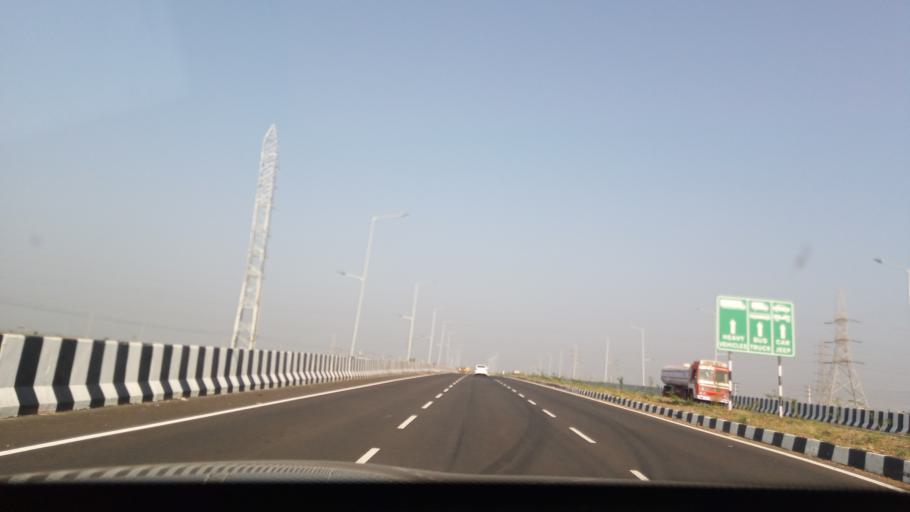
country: IN
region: Karnataka
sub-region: Haveri
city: Ranibennur
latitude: 14.6071
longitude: 75.6170
